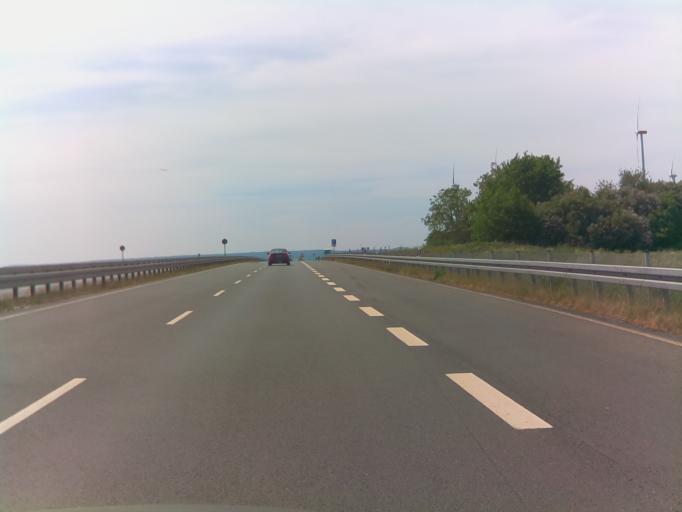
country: DE
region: Saxony-Anhalt
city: Wolmirsleben
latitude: 51.9784
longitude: 11.4741
